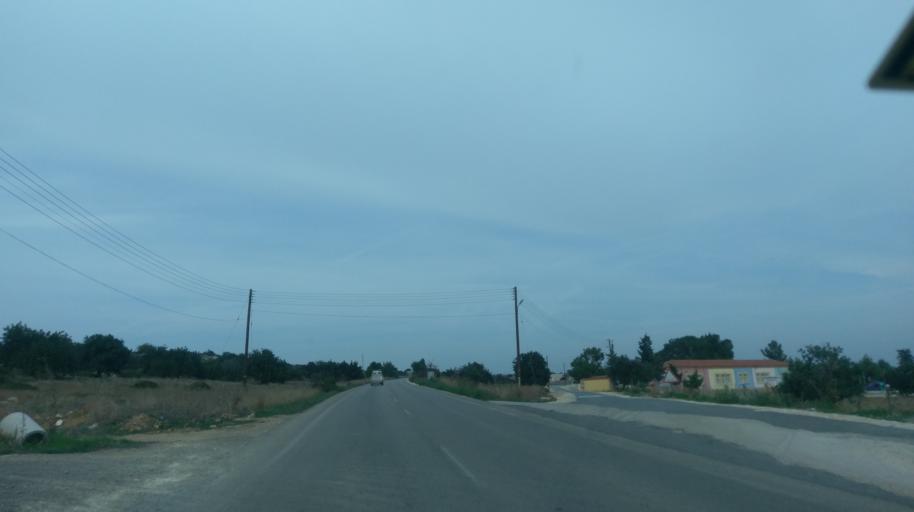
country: CY
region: Ammochostos
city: Leonarisso
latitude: 35.4233
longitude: 34.1260
